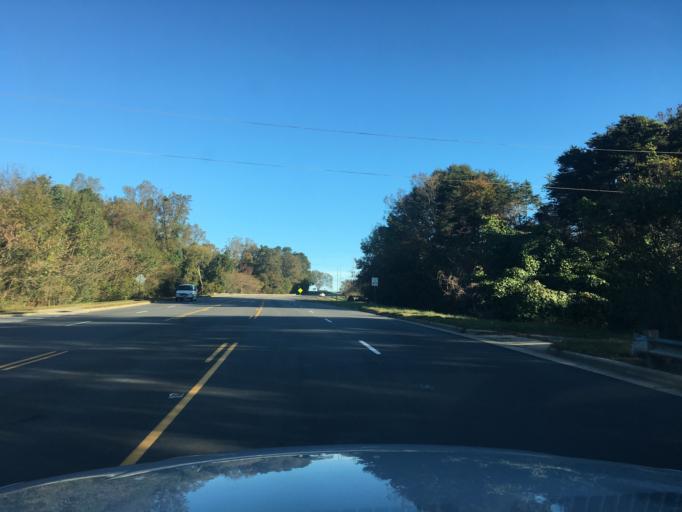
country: US
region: North Carolina
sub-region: Catawba County
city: Hickory
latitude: 35.7105
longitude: -81.3447
